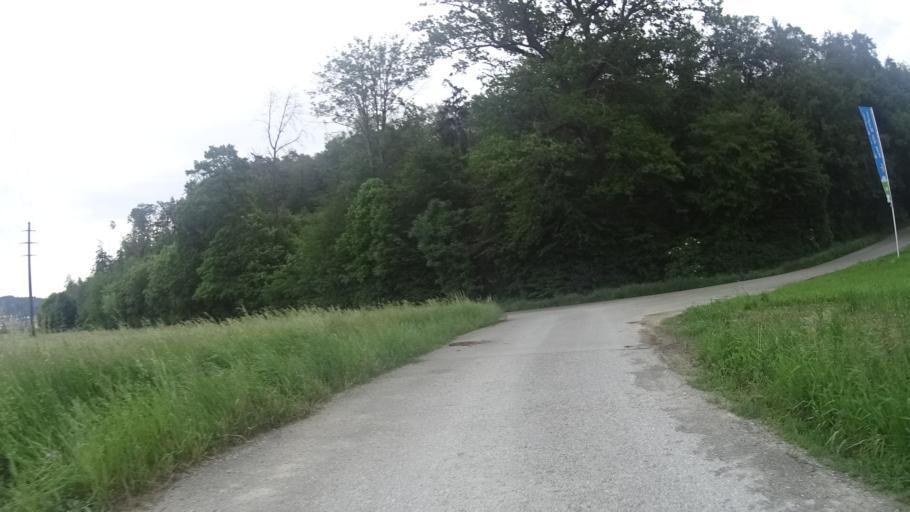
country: DE
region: Baden-Wuerttemberg
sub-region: Freiburg Region
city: Waldshut-Tiengen
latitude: 47.6092
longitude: 8.1970
